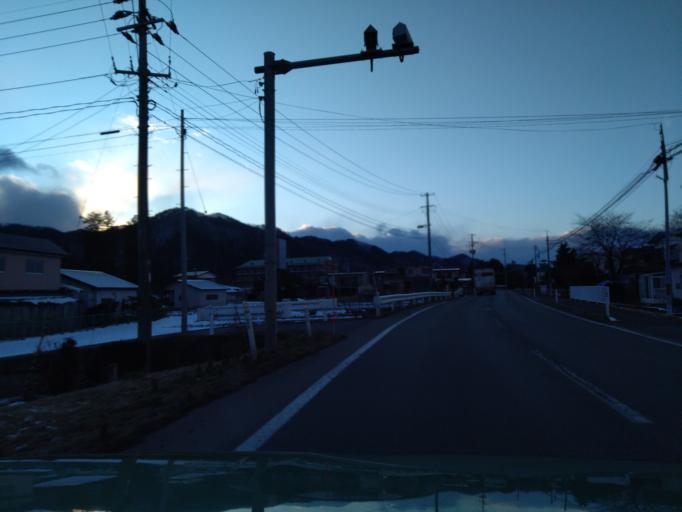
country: JP
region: Iwate
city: Shizukuishi
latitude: 39.6907
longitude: 141.0688
